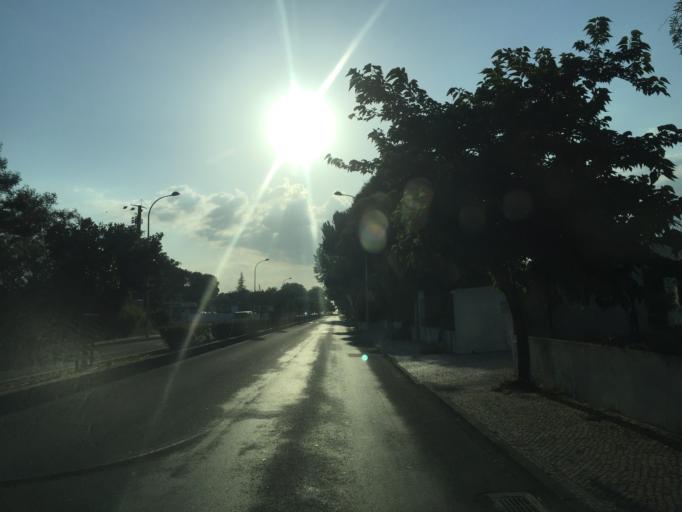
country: PT
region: Santarem
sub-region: Torres Novas
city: Torres Novas
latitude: 39.4731
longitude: -8.5500
